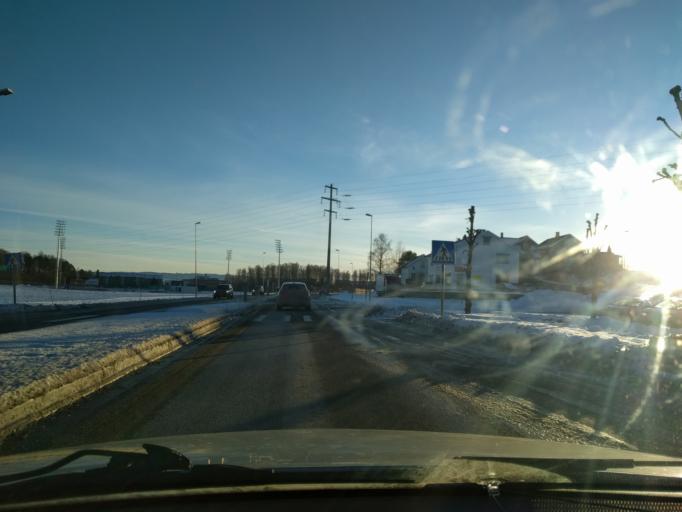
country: NO
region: Hedmark
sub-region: Hamar
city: Hamar
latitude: 60.8086
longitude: 11.0885
